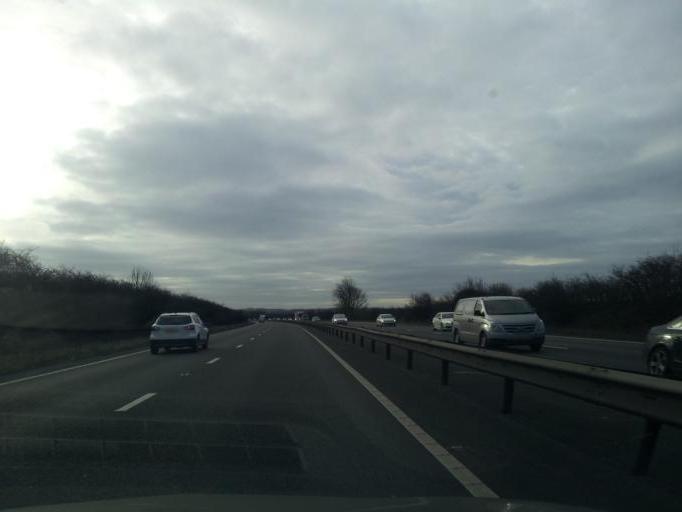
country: GB
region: England
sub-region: Lincolnshire
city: Long Bennington
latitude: 52.9879
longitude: -0.7608
